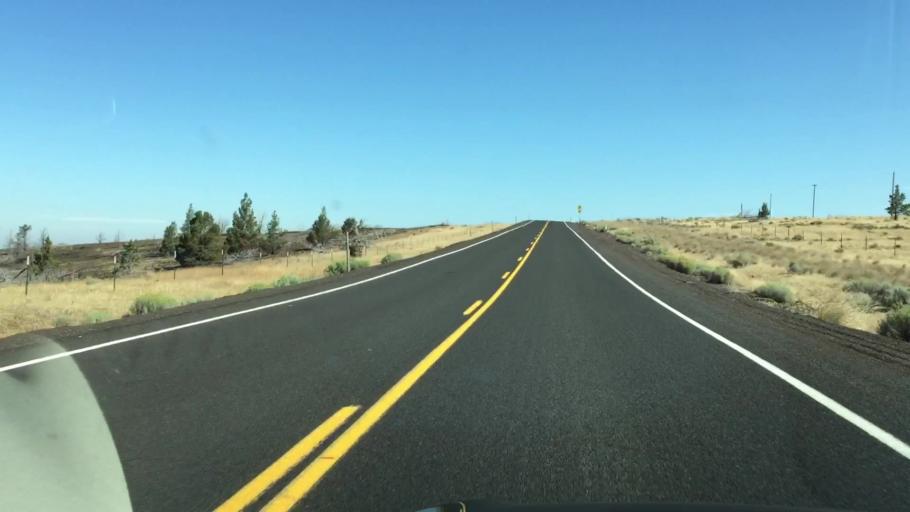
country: US
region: Oregon
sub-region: Jefferson County
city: Warm Springs
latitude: 45.0135
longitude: -120.9903
